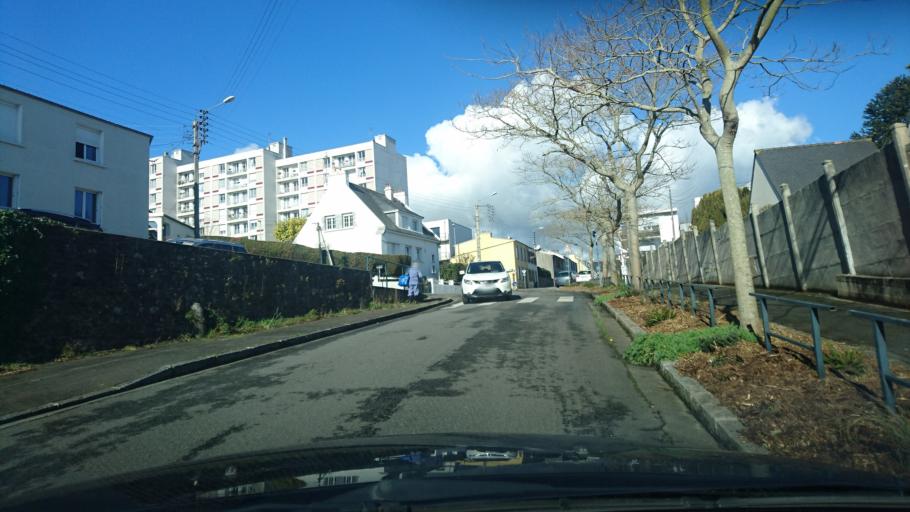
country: FR
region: Brittany
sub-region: Departement du Finistere
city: Brest
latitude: 48.3956
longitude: -4.4576
